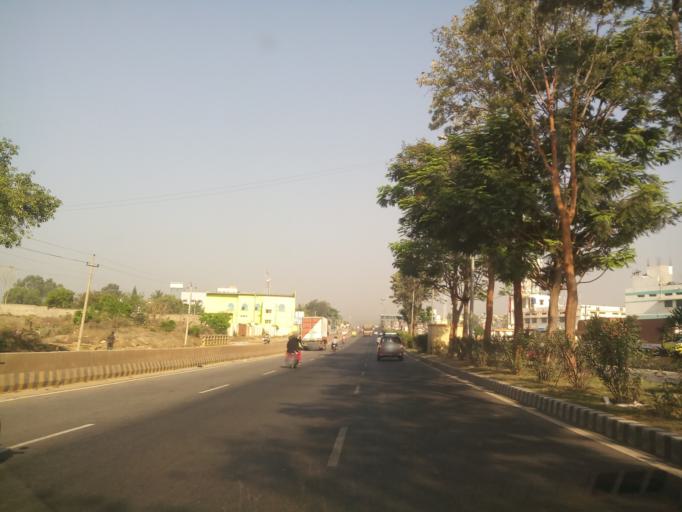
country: IN
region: Karnataka
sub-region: Bangalore Rural
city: Nelamangala
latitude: 13.0891
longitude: 77.4035
